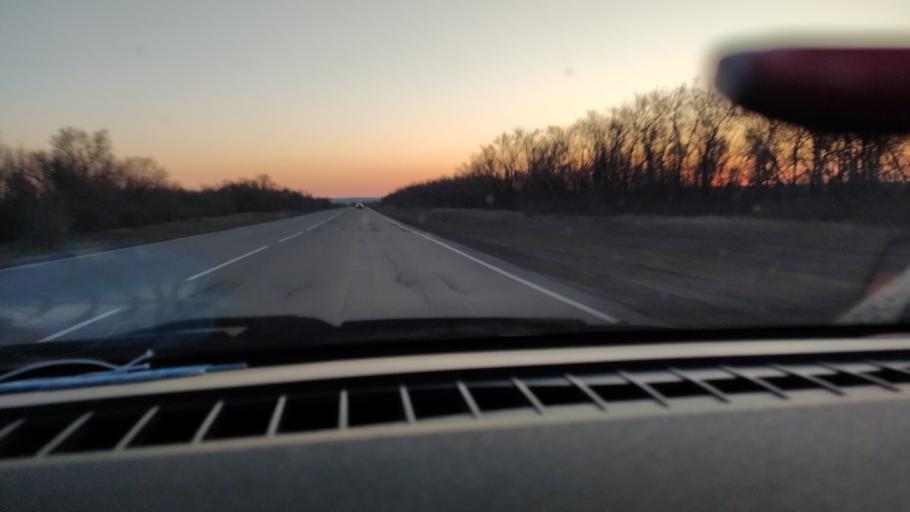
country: RU
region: Saratov
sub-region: Saratovskiy Rayon
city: Saratov
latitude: 51.7096
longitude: 46.0175
